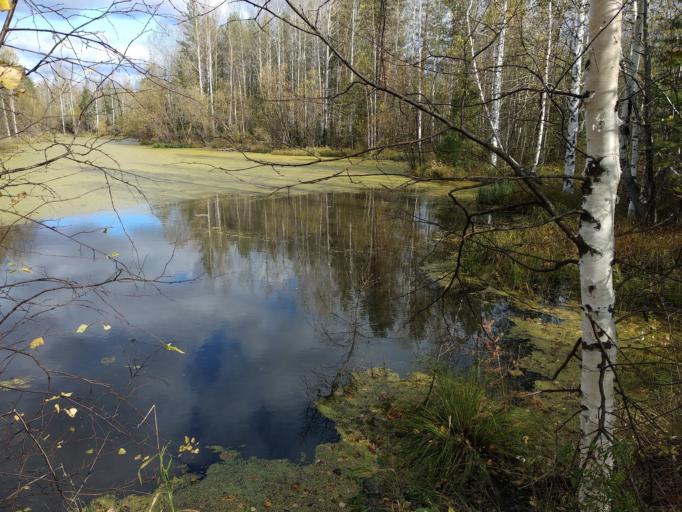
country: RU
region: Sverdlovsk
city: Rudnichnyy
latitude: 59.9544
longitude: 60.4732
